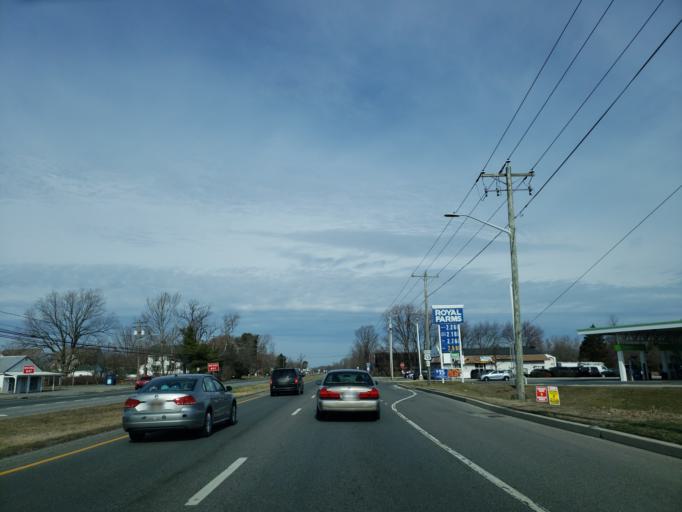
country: US
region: Delaware
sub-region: Kent County
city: Cheswold
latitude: 39.2240
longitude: -75.5765
